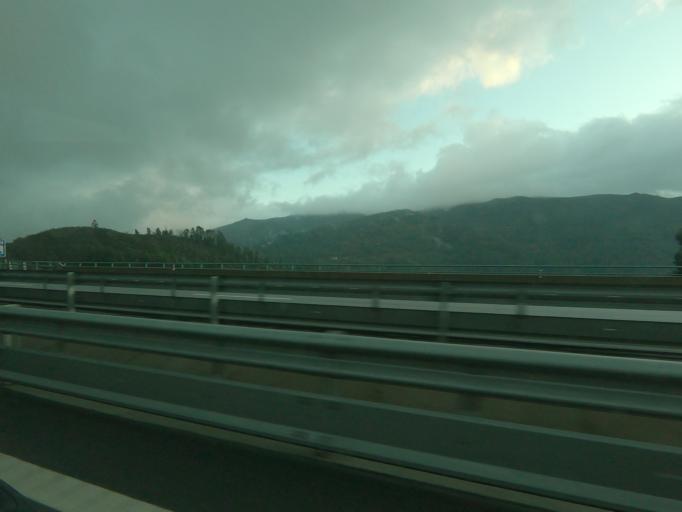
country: PT
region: Porto
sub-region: Baiao
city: Valadares
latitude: 41.2536
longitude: -7.9759
